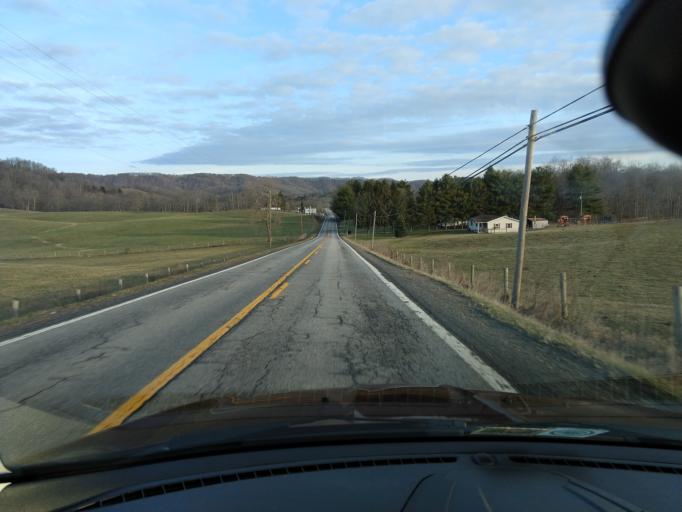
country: US
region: West Virginia
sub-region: Greenbrier County
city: Lewisburg
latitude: 37.9636
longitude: -80.3802
